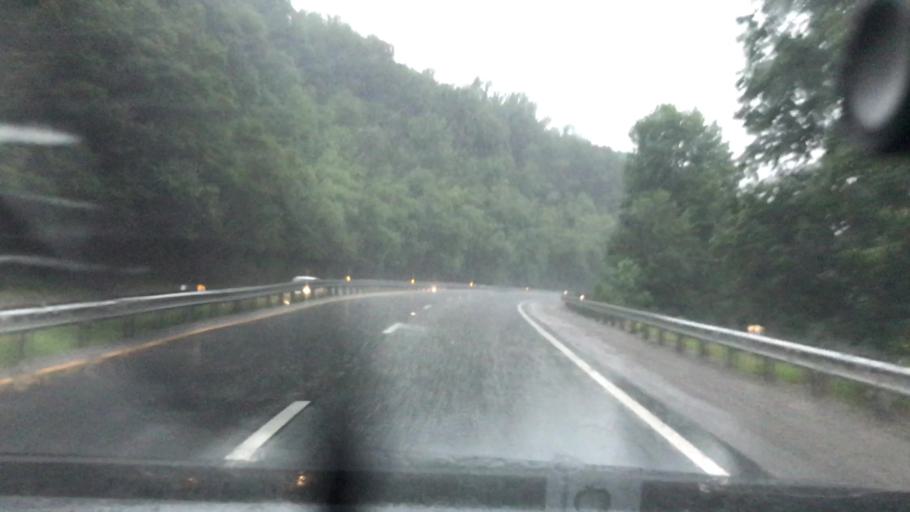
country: US
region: Virginia
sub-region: Giles County
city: Pearisburg
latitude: 37.3470
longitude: -80.7602
